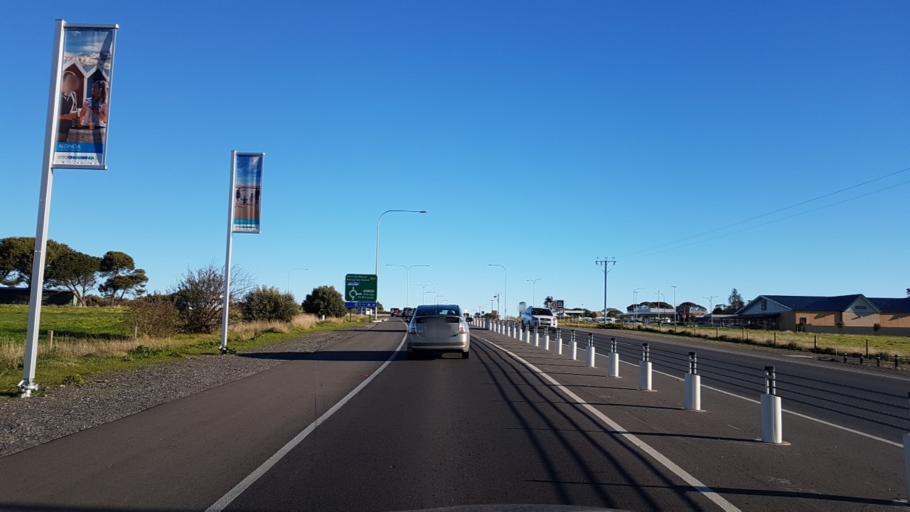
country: AU
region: South Australia
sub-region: Onkaparinga
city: Aldinga
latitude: -35.2662
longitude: 138.4862
